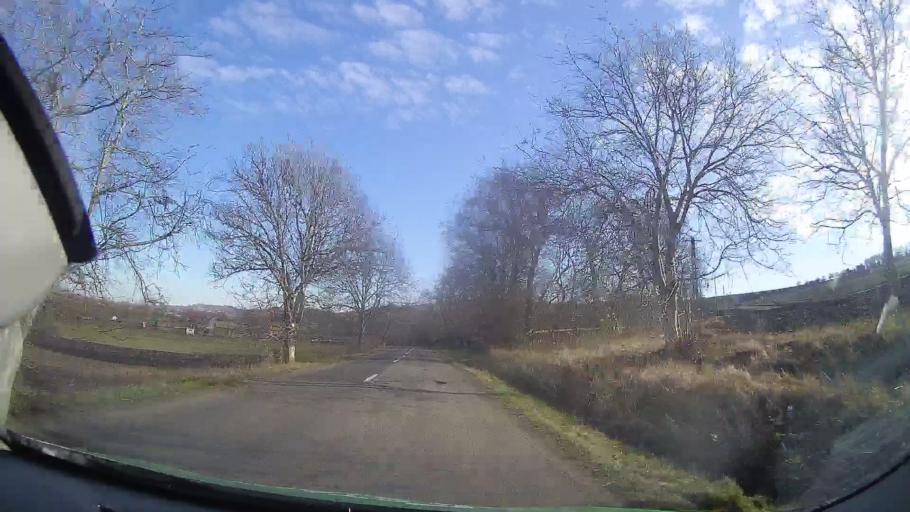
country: RO
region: Mures
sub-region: Comuna Iclanzel
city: Iclanzel
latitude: 46.5262
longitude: 24.2845
